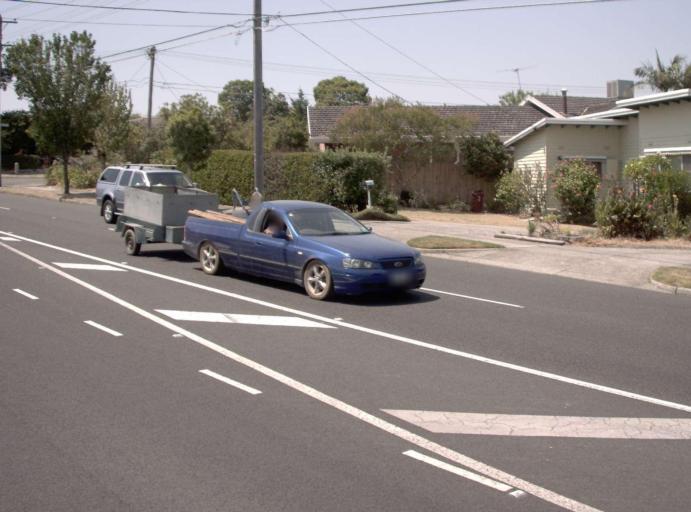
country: AU
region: Victoria
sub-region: Manningham
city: Bulleen
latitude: -37.7756
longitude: 145.0900
